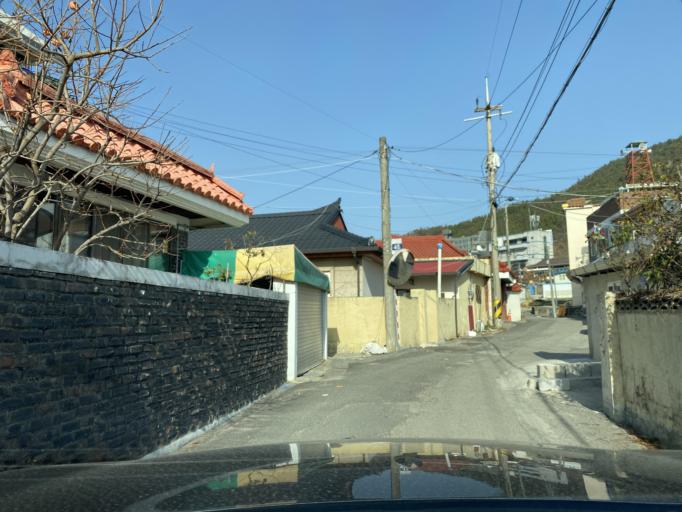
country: KR
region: Chungcheongnam-do
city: Yesan
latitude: 36.6835
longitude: 126.8462
